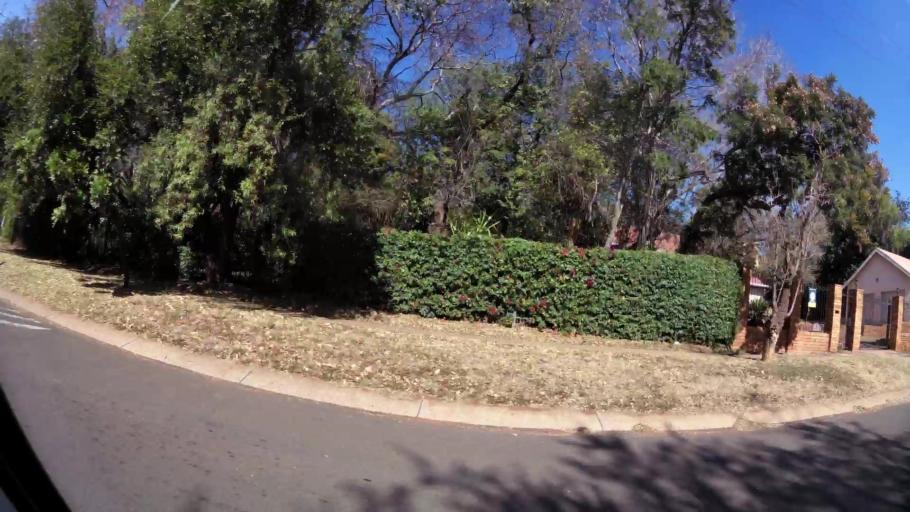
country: ZA
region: Gauteng
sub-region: City of Tshwane Metropolitan Municipality
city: Pretoria
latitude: -25.7751
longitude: 28.2159
